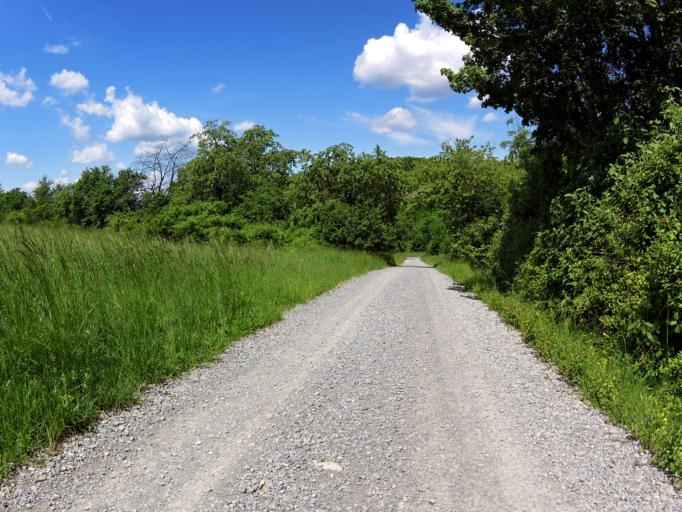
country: DE
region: Bavaria
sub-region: Regierungsbezirk Unterfranken
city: Theilheim
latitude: 49.7300
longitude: 10.0251
